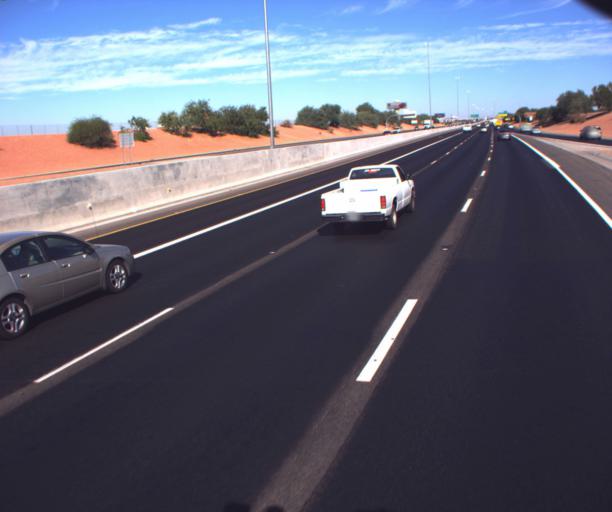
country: US
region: Arizona
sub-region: Maricopa County
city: Tolleson
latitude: 33.4968
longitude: -112.2646
